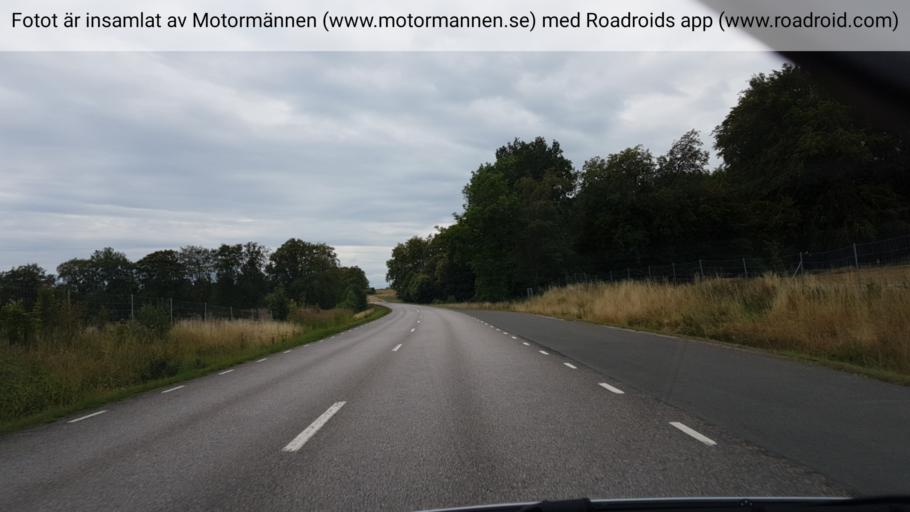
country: SE
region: Vaestra Goetaland
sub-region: Hjo Kommun
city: Hjo
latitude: 58.3431
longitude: 14.3410
